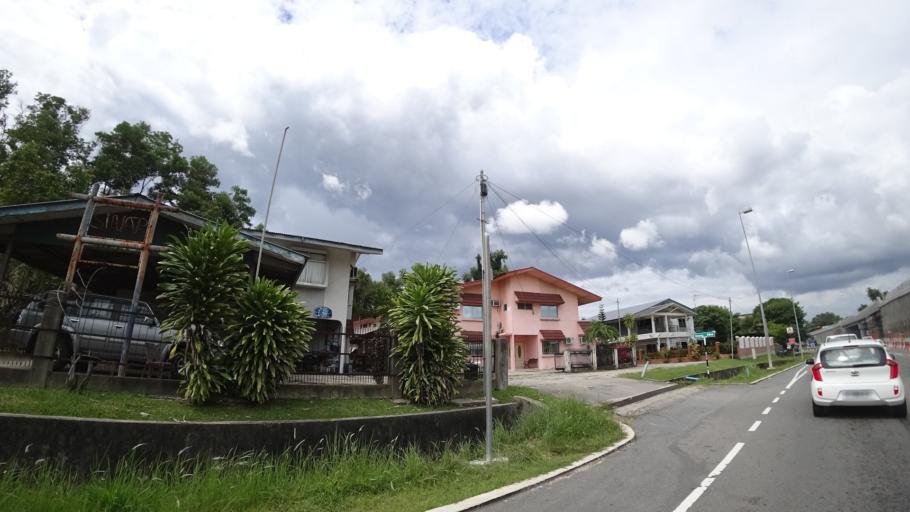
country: BN
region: Brunei and Muara
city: Bandar Seri Begawan
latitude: 4.8821
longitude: 114.8915
